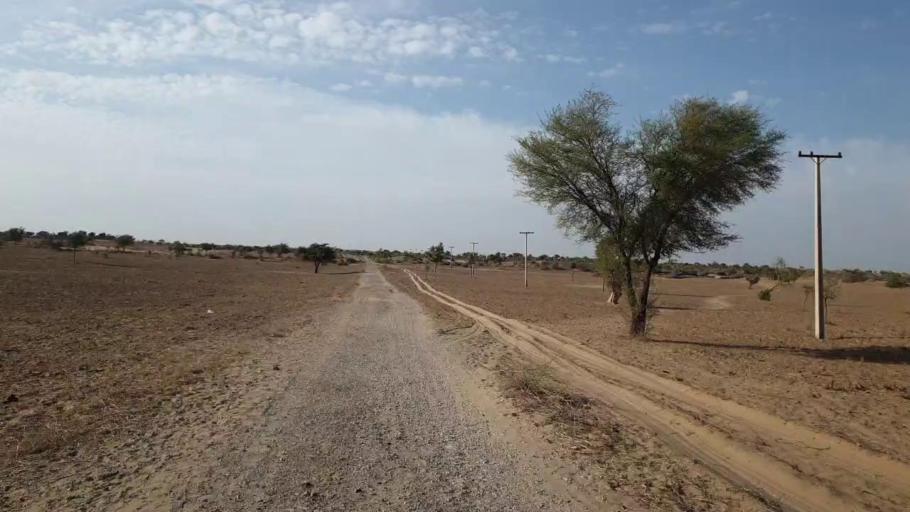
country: PK
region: Sindh
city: Nabisar
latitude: 25.0482
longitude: 69.9715
